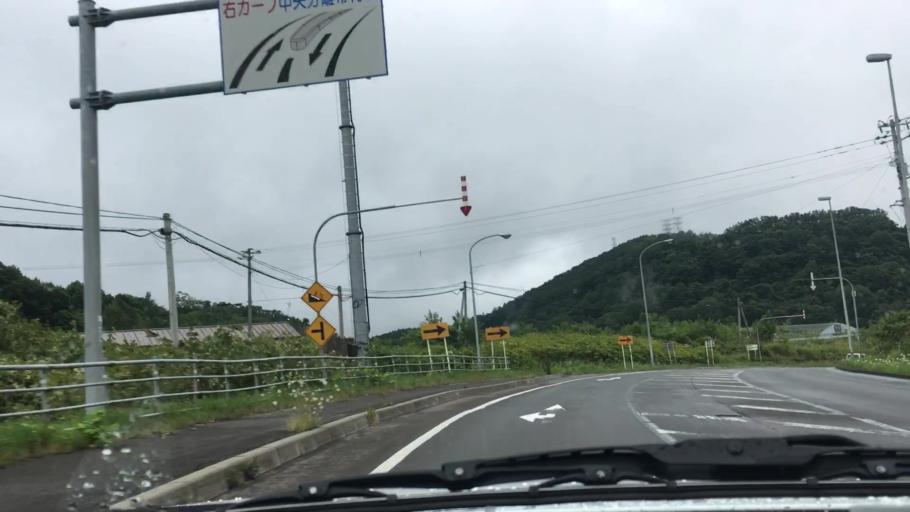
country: JP
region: Hokkaido
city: Niseko Town
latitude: 42.6075
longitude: 140.7287
